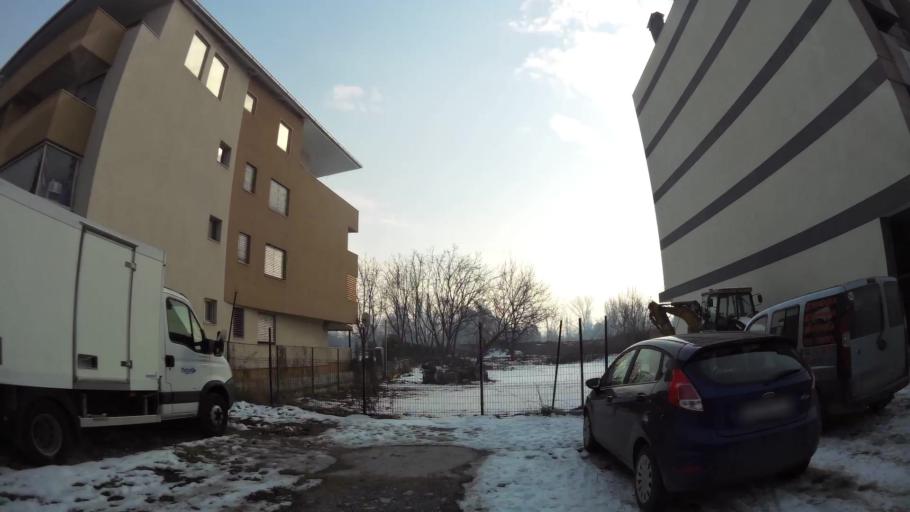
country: MK
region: Karpos
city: Skopje
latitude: 42.0128
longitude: 21.4113
